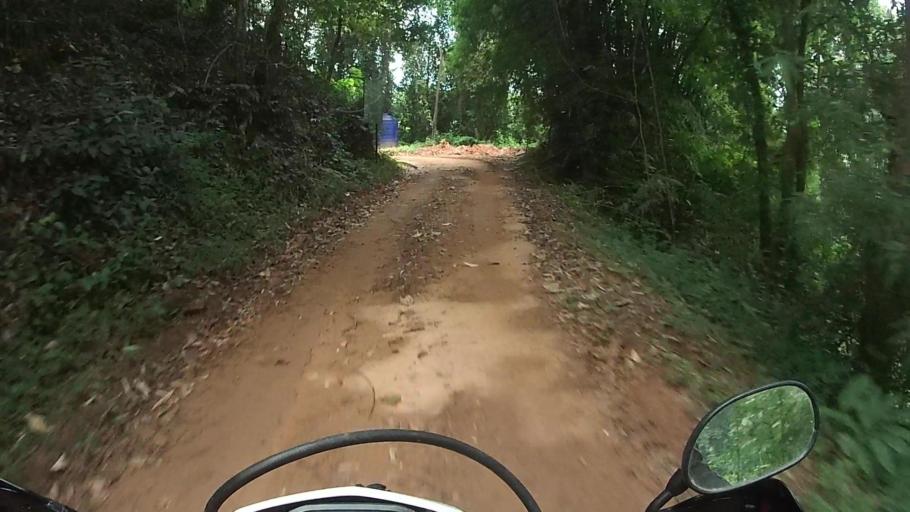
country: TH
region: Chiang Mai
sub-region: Amphoe Chiang Dao
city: Chiang Dao
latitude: 19.3187
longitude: 98.8815
